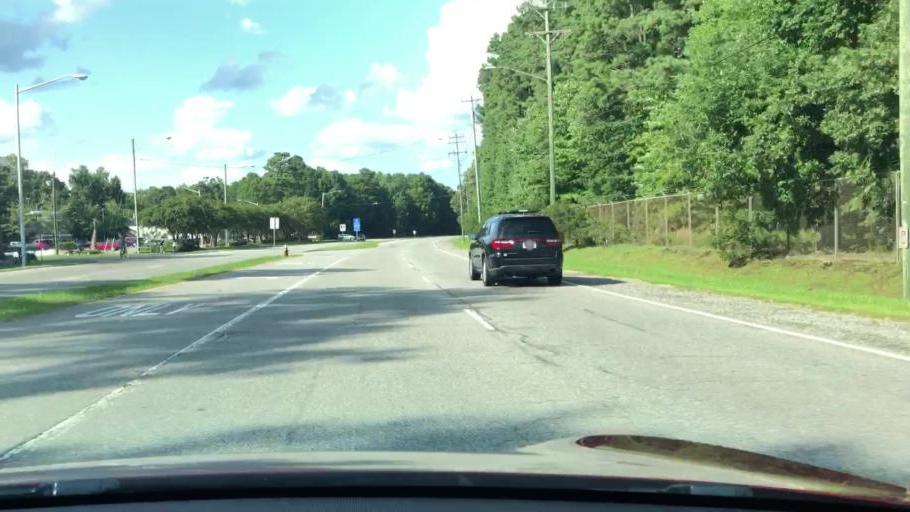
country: US
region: Virginia
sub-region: City of Virginia Beach
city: Virginia Beach
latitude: 36.8131
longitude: -75.9889
